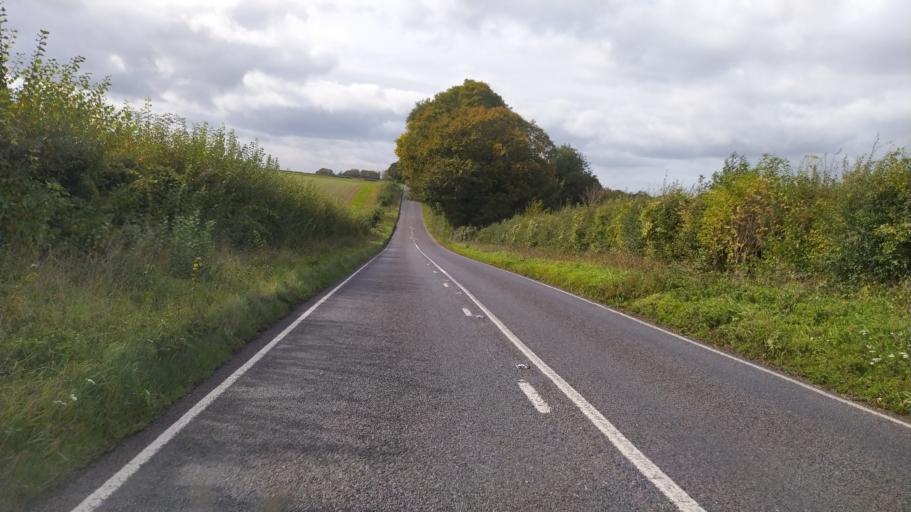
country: GB
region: England
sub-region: Hampshire
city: Andover
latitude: 51.1209
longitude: -1.4590
